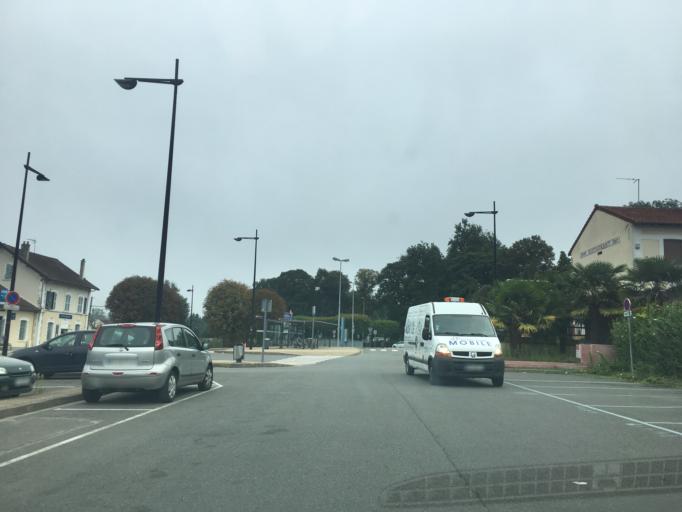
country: FR
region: Ile-de-France
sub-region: Departement de l'Essonne
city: Mennecy
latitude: 48.5704
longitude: 2.4329
